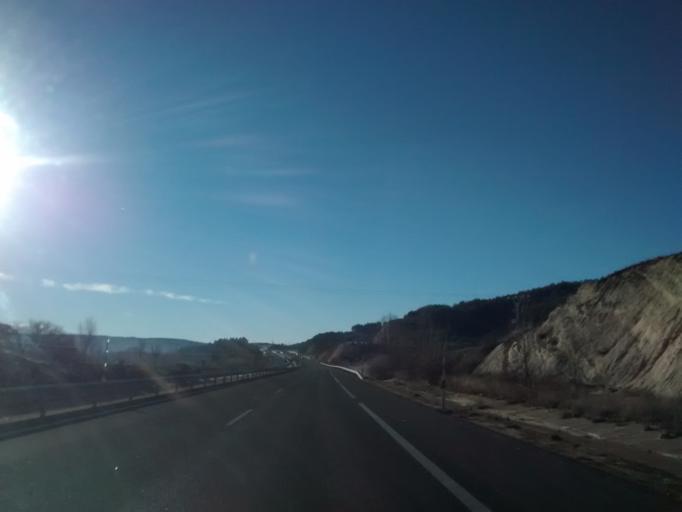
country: ES
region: Castille and Leon
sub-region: Provincia de Palencia
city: Aguilar de Campoo
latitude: 42.7392
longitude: -4.2896
